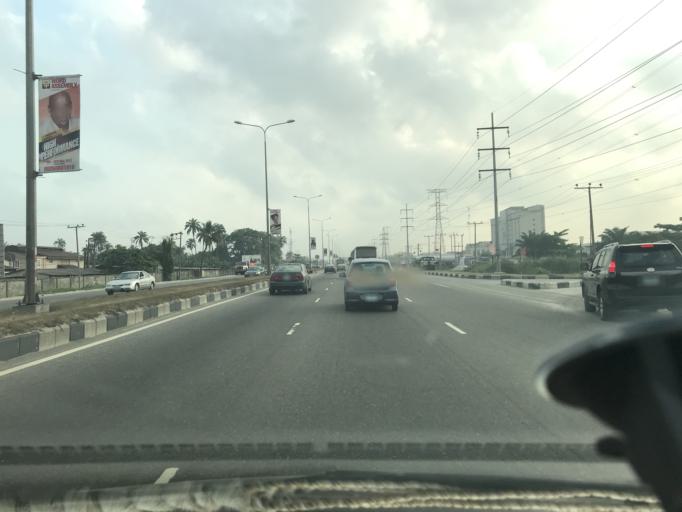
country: NG
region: Lagos
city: Ikoyi
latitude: 6.4470
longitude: 3.5448
